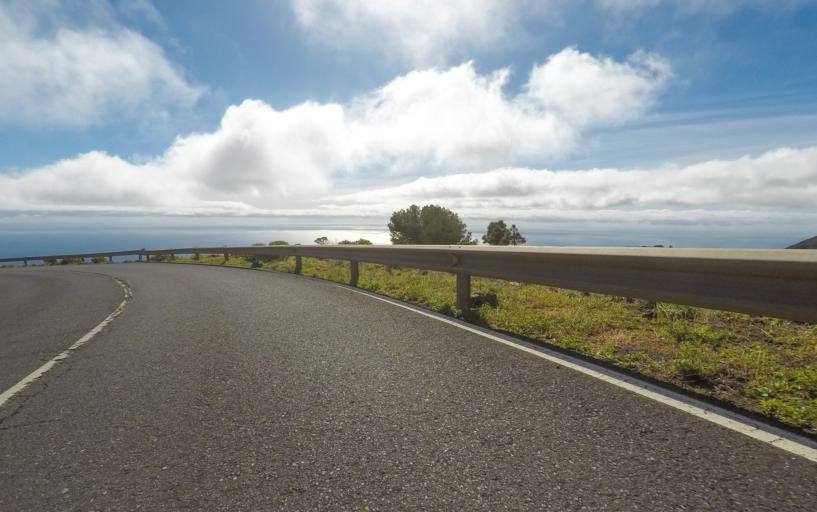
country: ES
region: Canary Islands
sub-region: Provincia de Santa Cruz de Tenerife
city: San Sebastian de la Gomera
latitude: 28.0947
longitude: -17.1741
